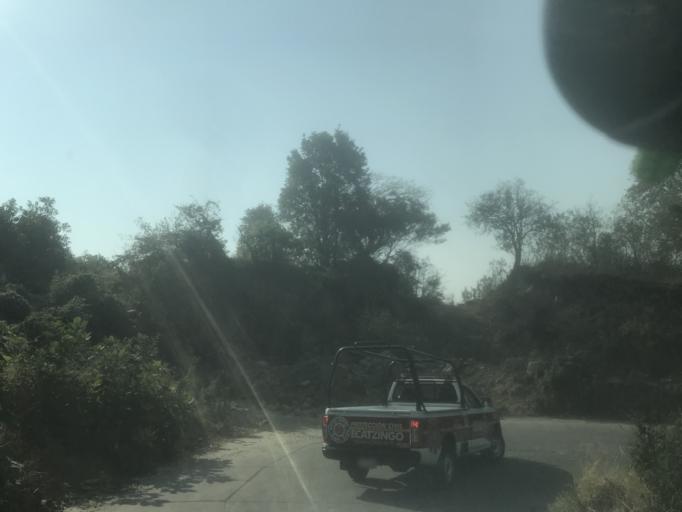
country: MX
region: Morelos
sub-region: Yecapixtla
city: Texcala
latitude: 18.9379
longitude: -98.7939
